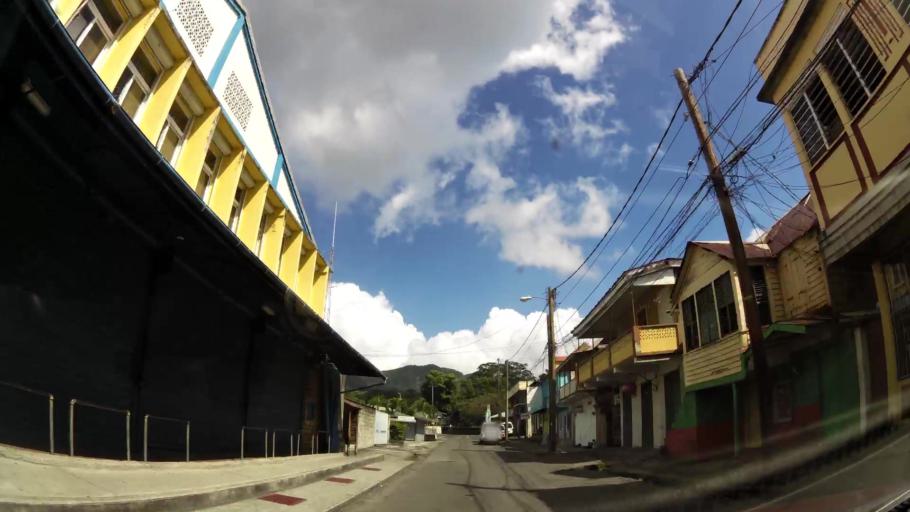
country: DM
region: Saint George
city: Roseau
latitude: 15.2994
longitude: -61.3849
